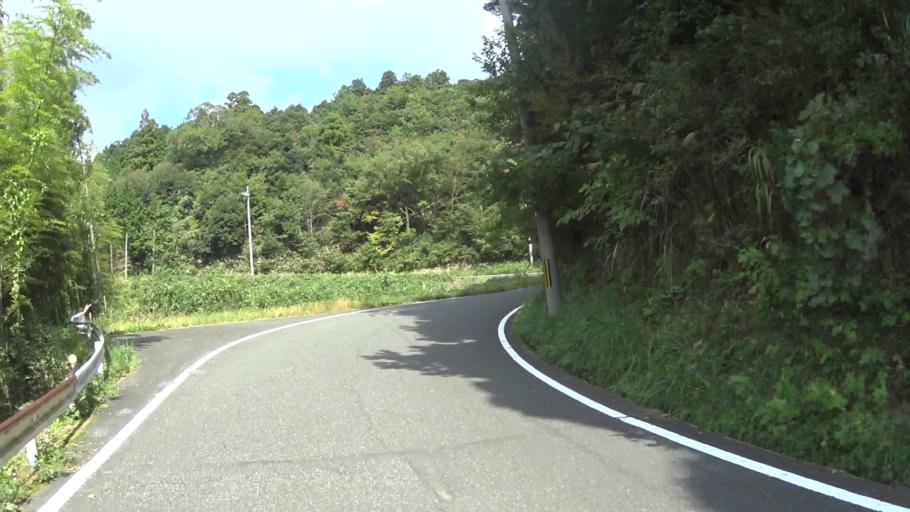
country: JP
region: Kyoto
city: Miyazu
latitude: 35.6797
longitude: 135.2676
